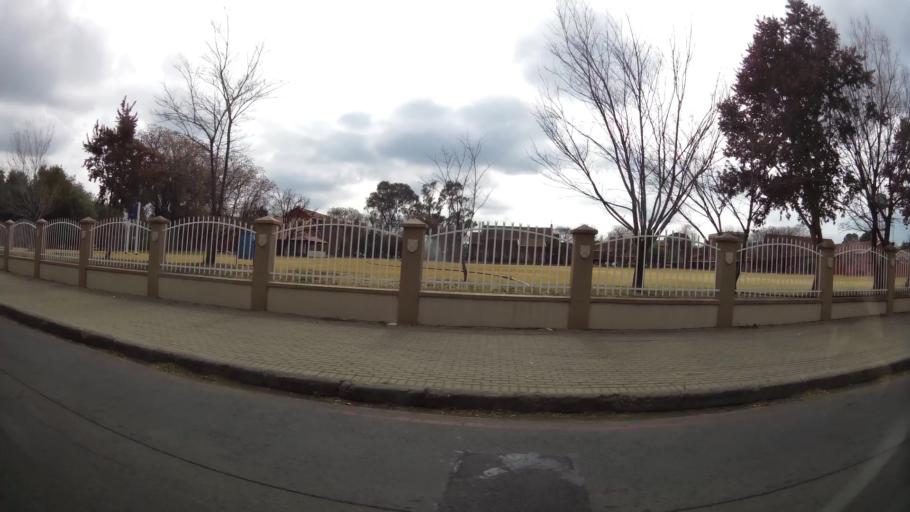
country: ZA
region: Orange Free State
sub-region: Mangaung Metropolitan Municipality
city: Bloemfontein
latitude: -29.1082
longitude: 26.2042
